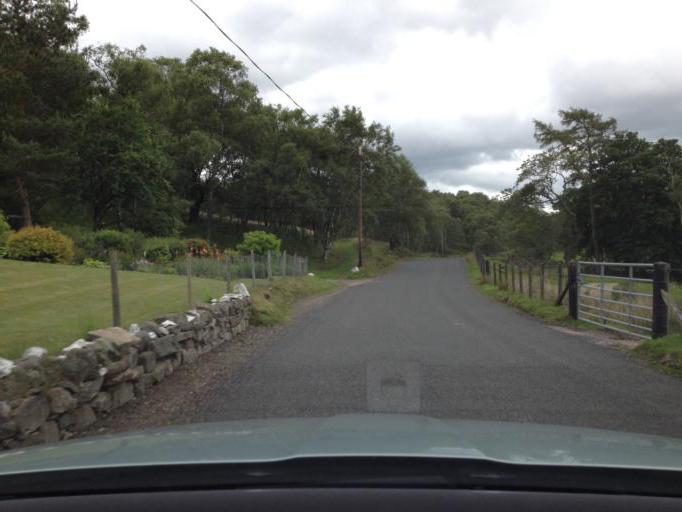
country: GB
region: Scotland
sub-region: Aberdeenshire
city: Aboyne
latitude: 56.8959
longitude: -2.7969
